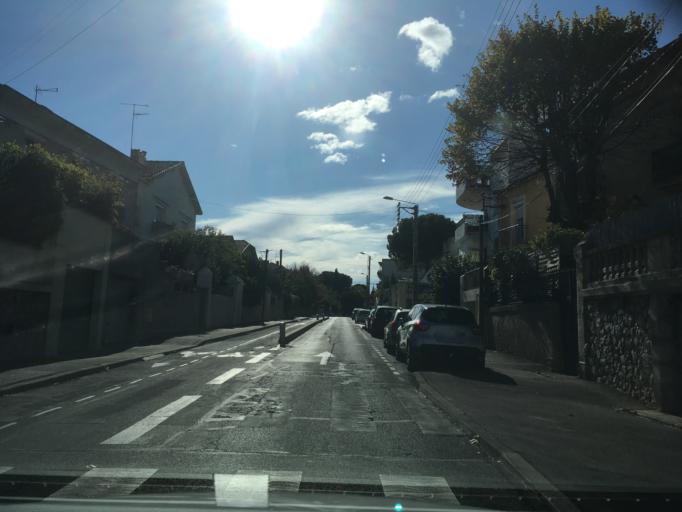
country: FR
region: Languedoc-Roussillon
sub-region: Departement de l'Herault
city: Montpellier
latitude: 43.5995
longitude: 3.8791
